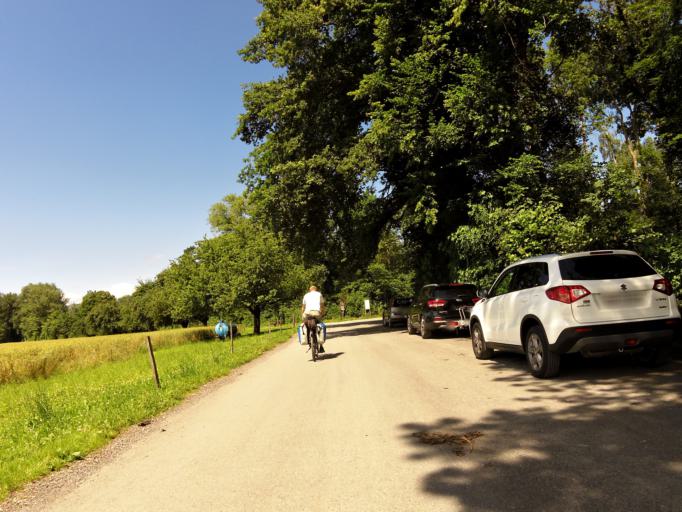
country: CH
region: Saint Gallen
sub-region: Wahlkreis Rheintal
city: Rheineck
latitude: 47.4816
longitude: 9.5802
